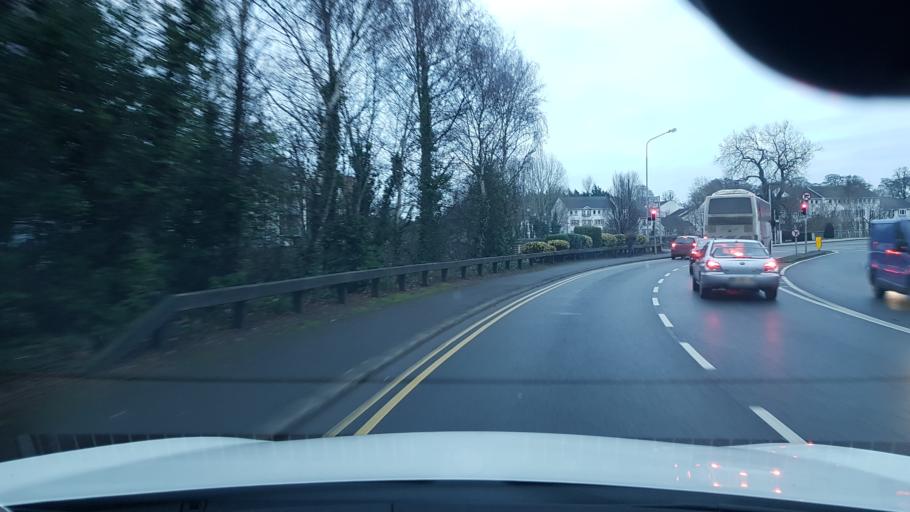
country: IE
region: Leinster
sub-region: An Mhi
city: Navan
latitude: 53.6552
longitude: -6.6833
